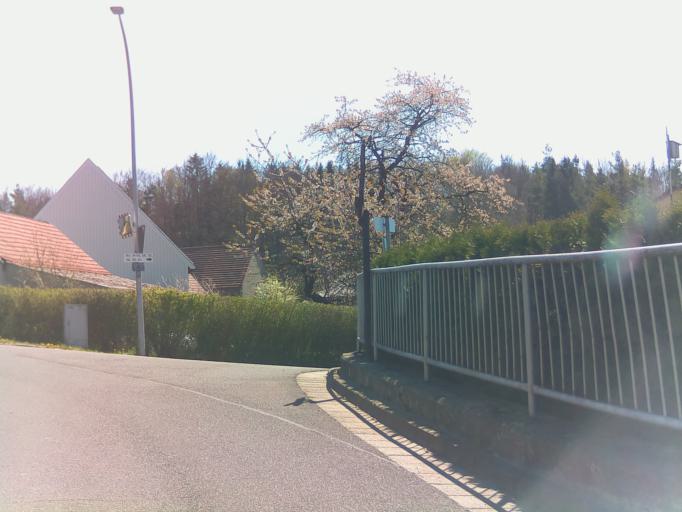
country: DE
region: Bavaria
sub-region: Upper Palatinate
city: Kastl
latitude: 49.4057
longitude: 11.6587
